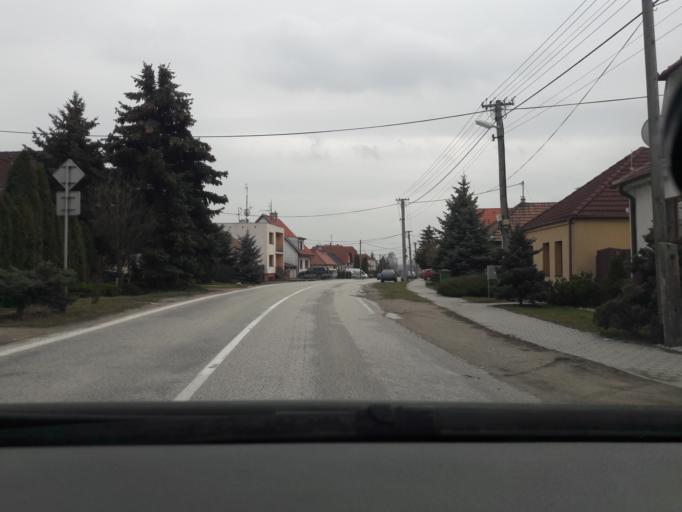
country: SK
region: Trnavsky
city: Smolenice
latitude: 48.4136
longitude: 17.3811
